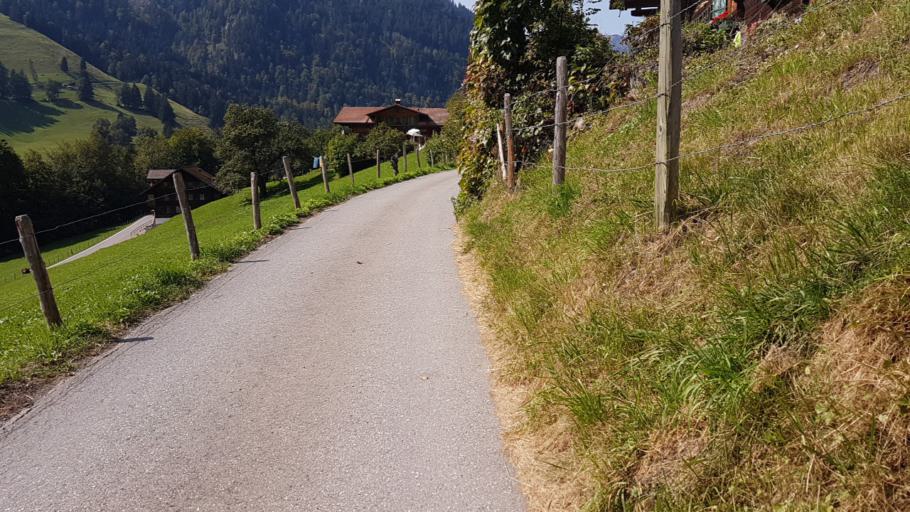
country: CH
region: Bern
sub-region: Frutigen-Niedersimmental District
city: Aeschi
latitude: 46.5909
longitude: 7.7224
